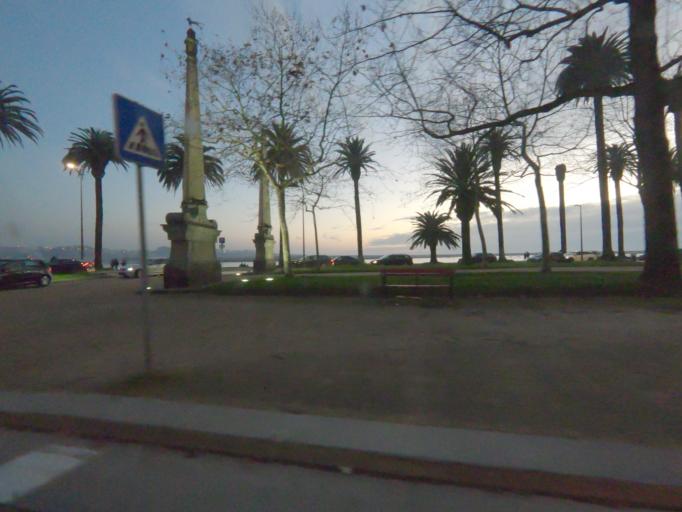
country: PT
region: Porto
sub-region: Vila Nova de Gaia
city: Canidelo
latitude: 41.1480
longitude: -8.6686
